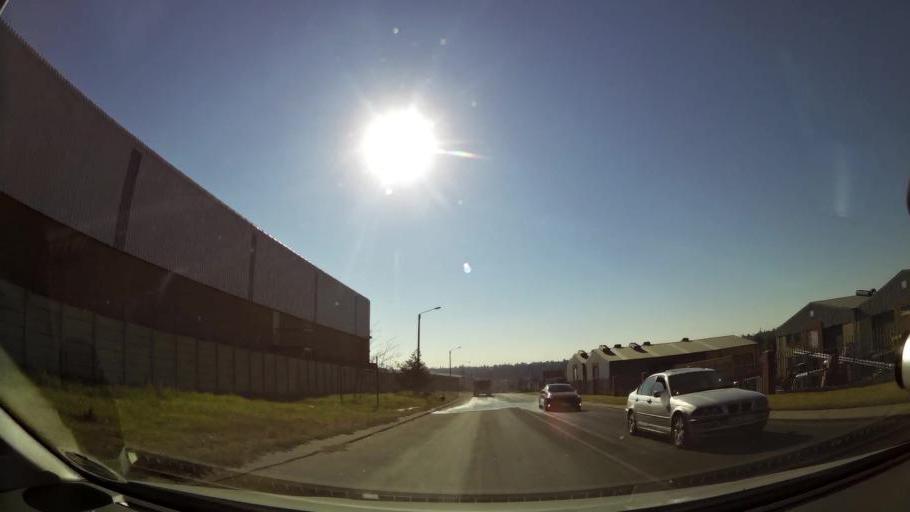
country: ZA
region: Gauteng
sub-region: City of Johannesburg Metropolitan Municipality
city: Modderfontein
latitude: -26.0681
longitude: 28.1931
